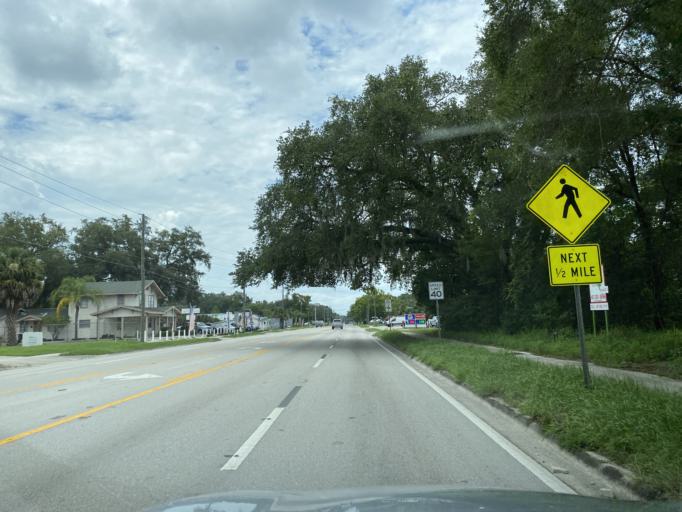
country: US
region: Florida
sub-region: Seminole County
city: Sanford
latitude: 28.7788
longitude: -81.2646
